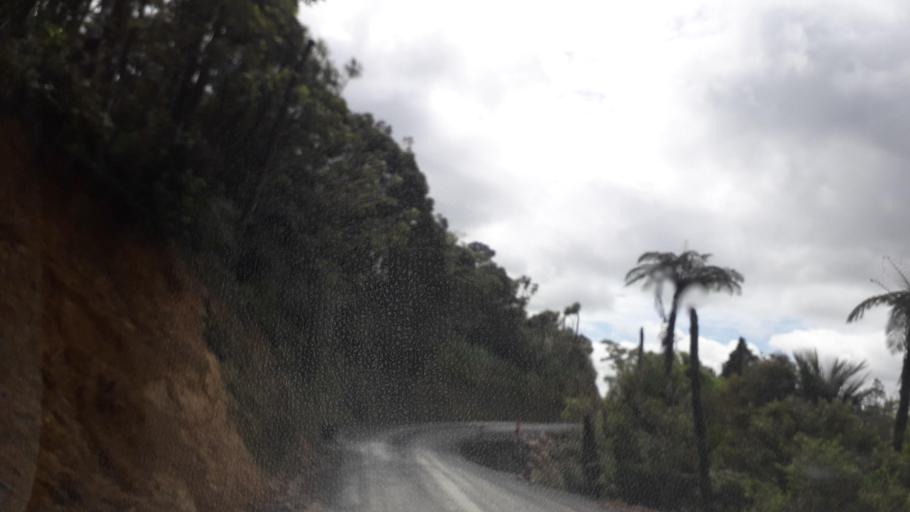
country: NZ
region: Northland
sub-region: Far North District
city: Kaitaia
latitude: -35.1924
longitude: 173.2867
